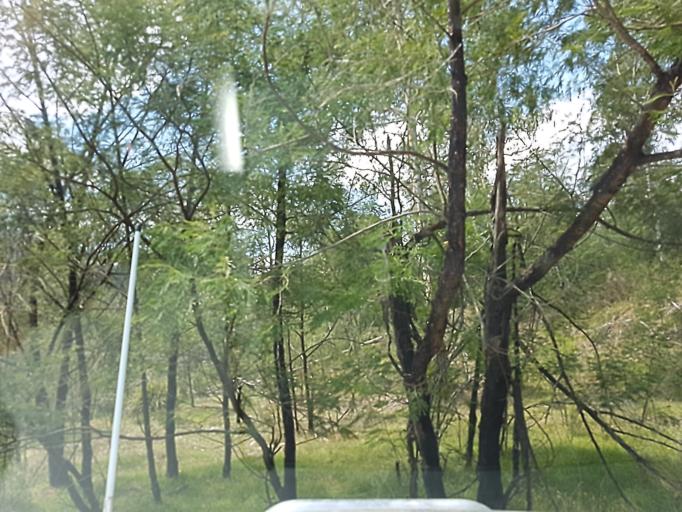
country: AU
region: Victoria
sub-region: East Gippsland
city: Lakes Entrance
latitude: -37.3933
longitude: 148.3336
